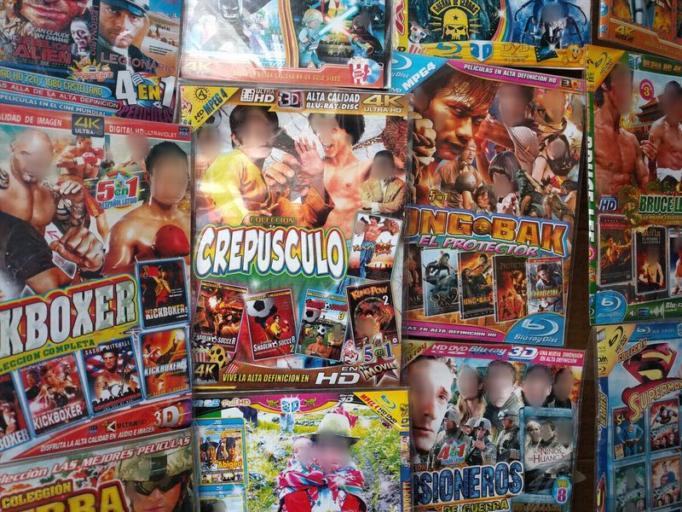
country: BO
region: Chuquisaca
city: Sucre
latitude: -19.0348
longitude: -65.2536
